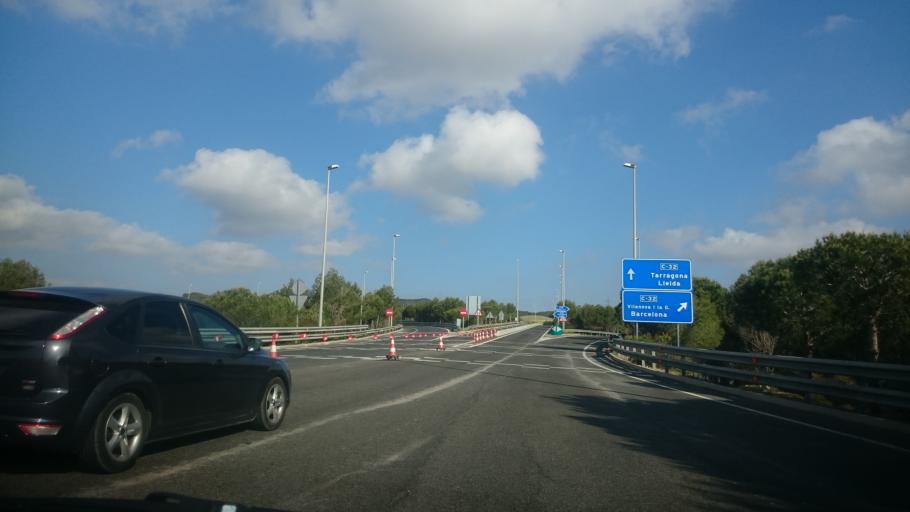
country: ES
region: Catalonia
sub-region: Provincia de Barcelona
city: Cubelles
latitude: 41.2067
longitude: 1.6587
